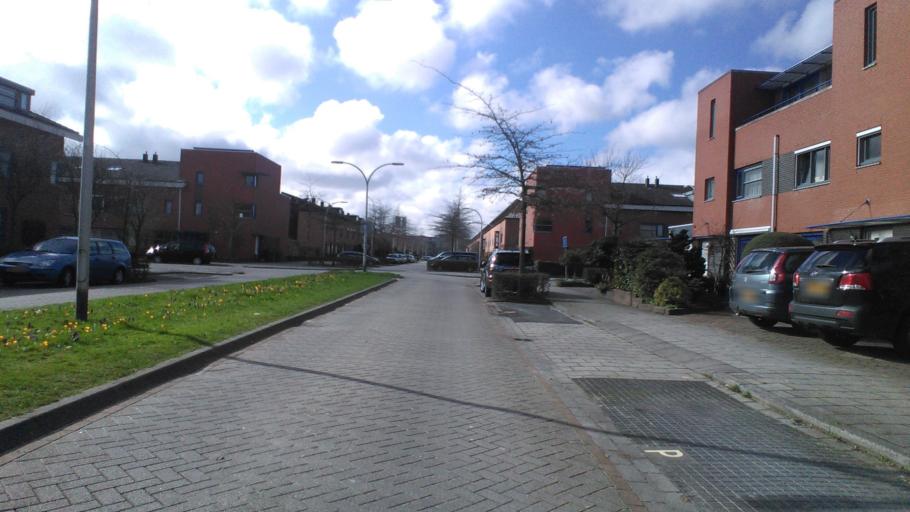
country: NL
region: South Holland
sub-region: Gemeente Pijnacker-Nootdorp
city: Pijnacker
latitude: 52.0079
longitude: 4.3940
